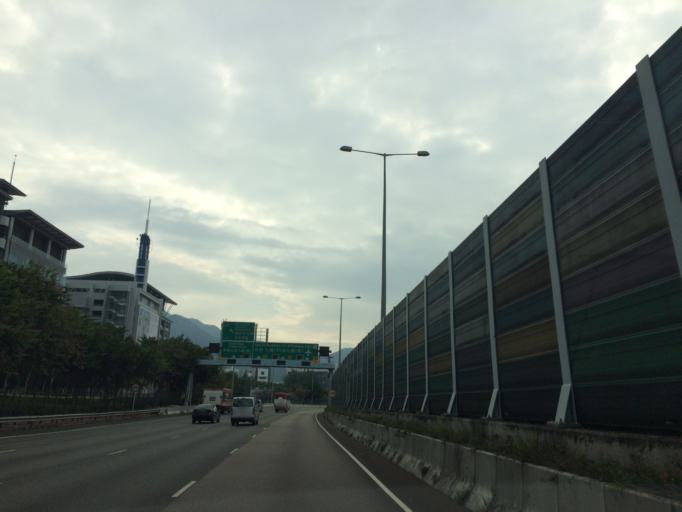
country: HK
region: Tai Po
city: Tai Po
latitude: 22.4249
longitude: 114.2102
